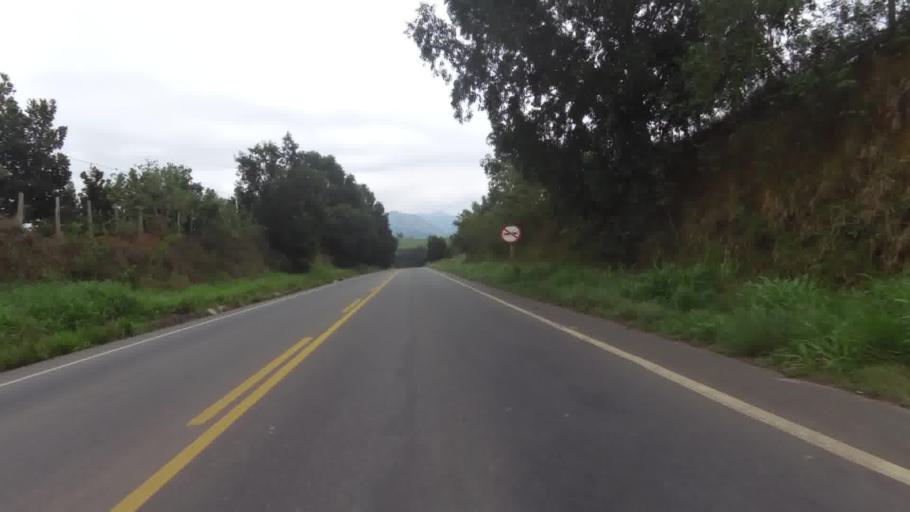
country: BR
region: Espirito Santo
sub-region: Iconha
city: Iconha
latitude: -20.7785
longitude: -40.7578
